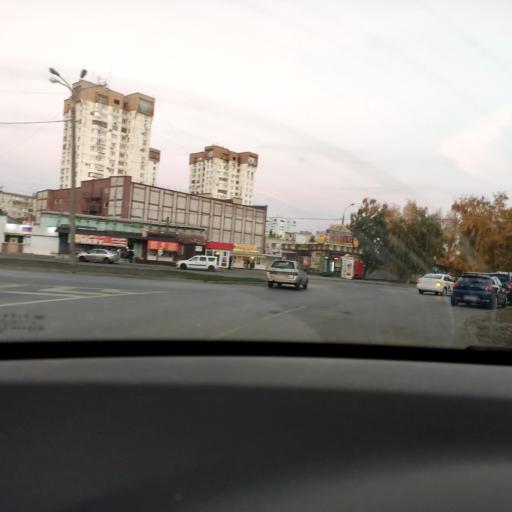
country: RU
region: Samara
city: Samara
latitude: 53.2609
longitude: 50.2287
